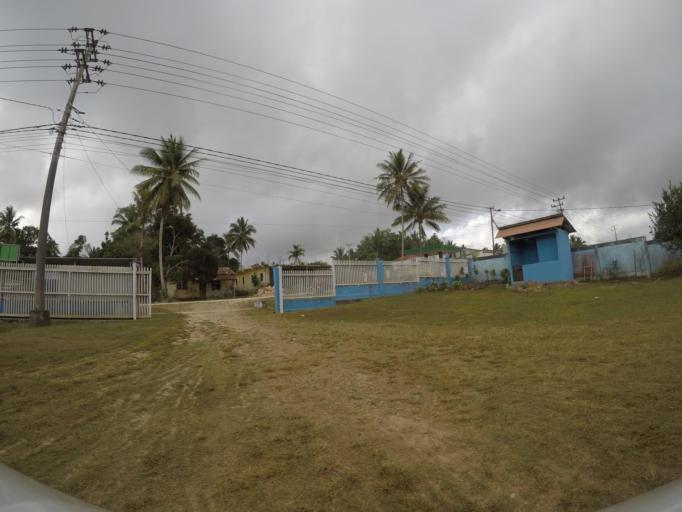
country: TL
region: Lautem
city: Lospalos
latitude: -8.5066
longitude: 126.9880
